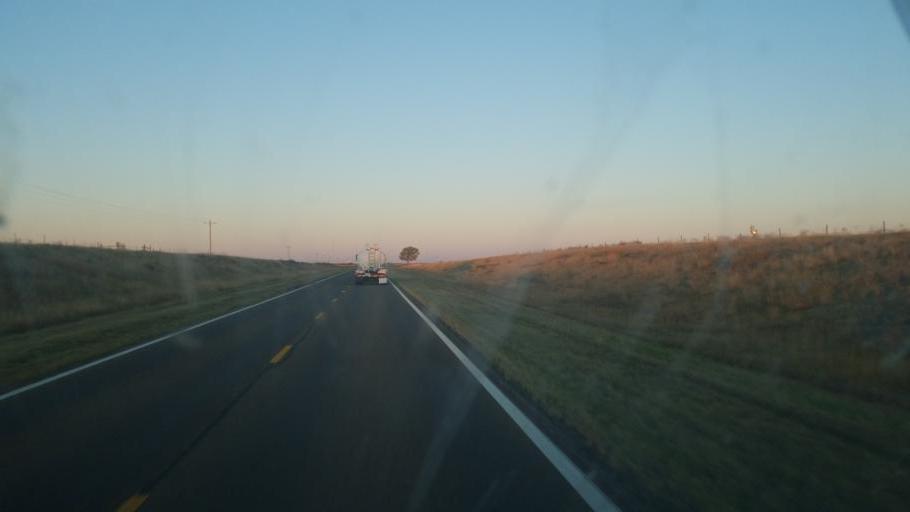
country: US
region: Kansas
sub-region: Wallace County
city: Sharon Springs
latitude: 38.9025
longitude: -101.7060
